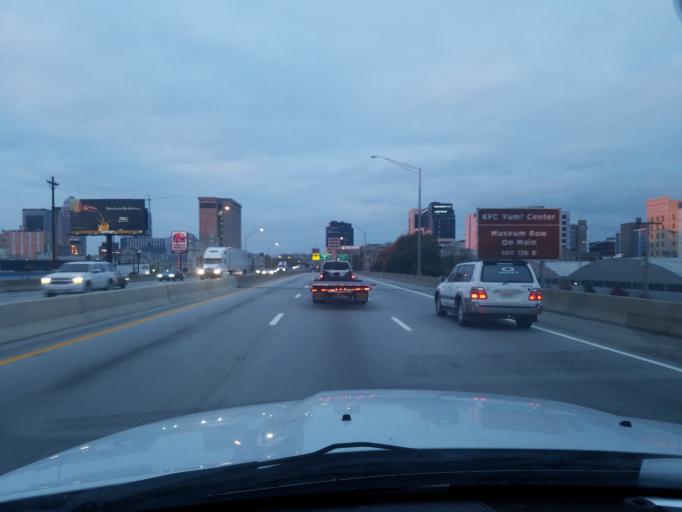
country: US
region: Kentucky
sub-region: Jefferson County
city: Louisville
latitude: 38.2437
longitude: -85.7525
